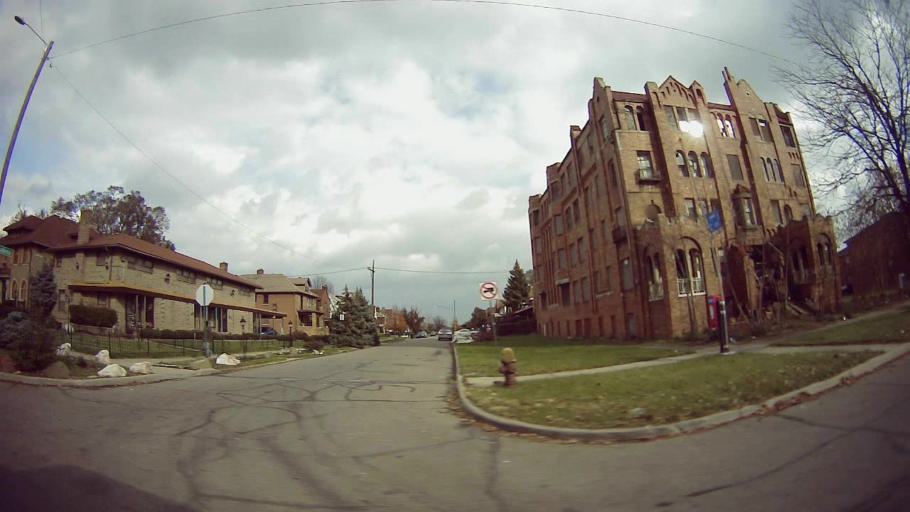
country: US
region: Michigan
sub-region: Wayne County
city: Highland Park
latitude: 42.3921
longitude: -83.1324
